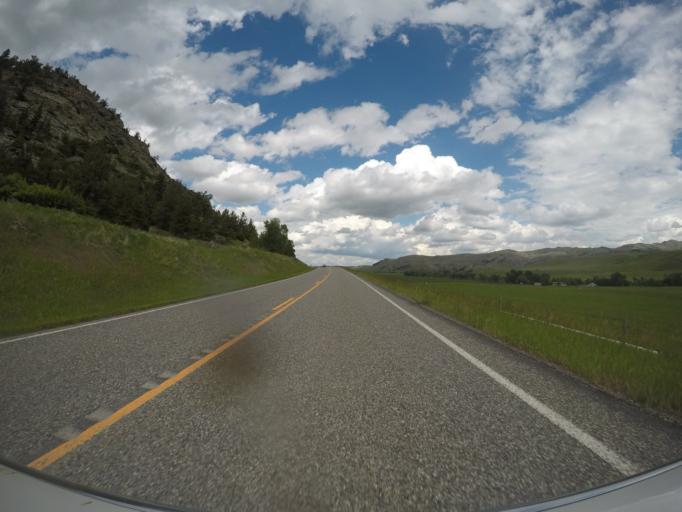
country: US
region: Montana
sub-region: Sweet Grass County
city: Big Timber
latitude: 45.6713
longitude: -110.0965
